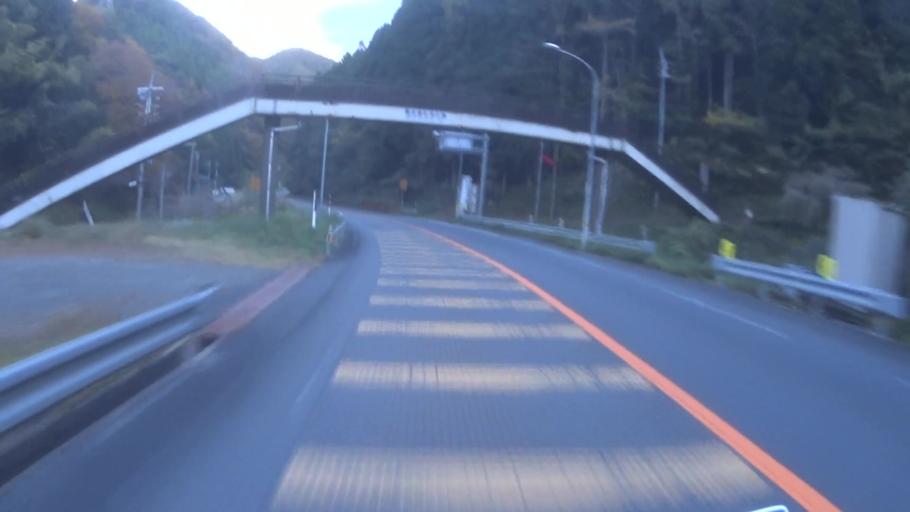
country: JP
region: Kyoto
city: Ayabe
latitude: 35.2377
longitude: 135.3210
